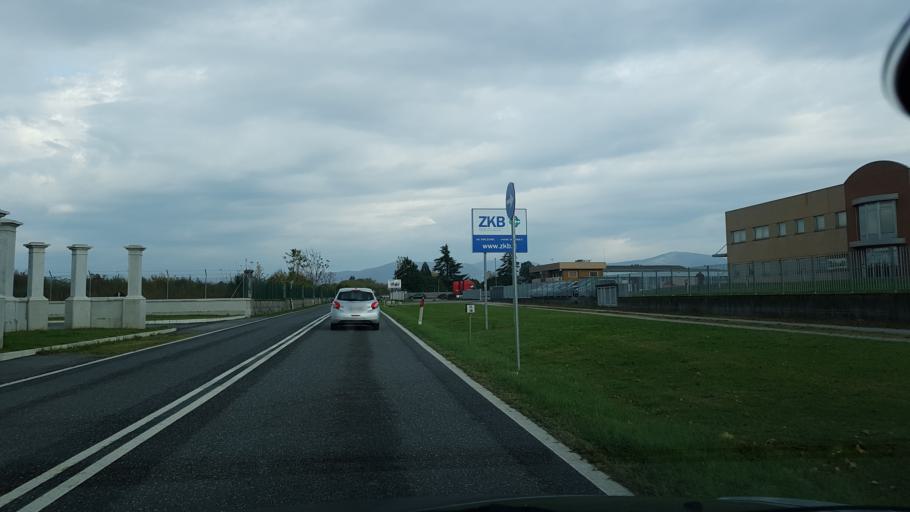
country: SI
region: Miren-Kostanjevica
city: Miren
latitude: 45.9021
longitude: 13.6094
